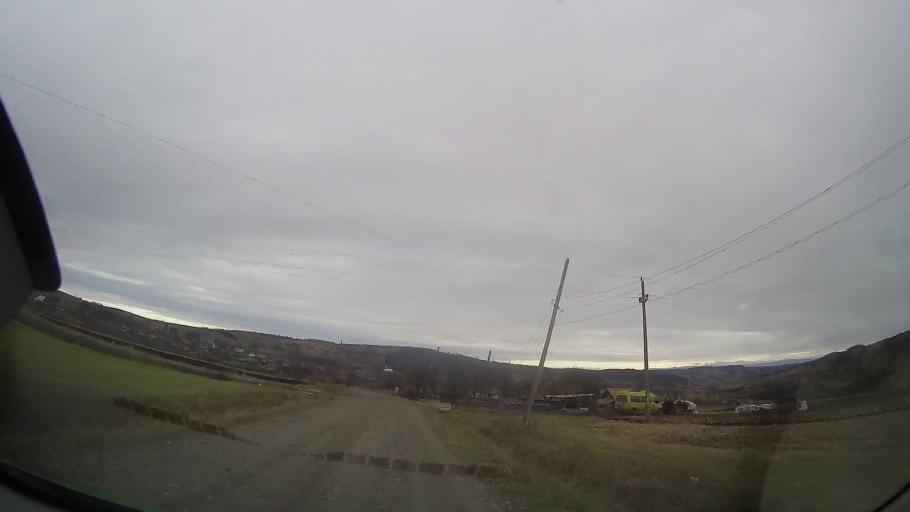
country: RO
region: Mures
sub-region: Comuna Bala
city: Bala
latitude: 46.7017
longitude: 24.4942
